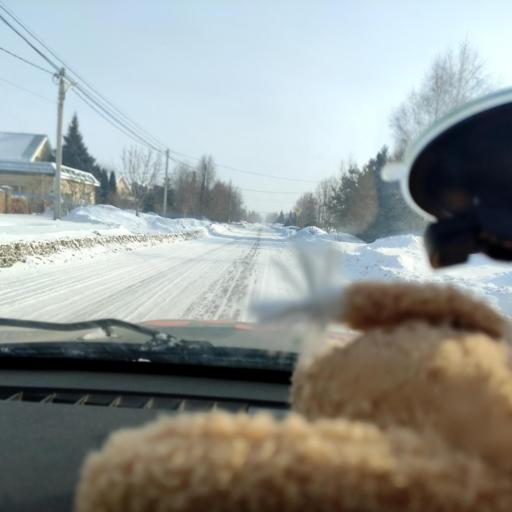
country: RU
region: Samara
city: Podstepki
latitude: 53.5114
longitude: 49.1440
